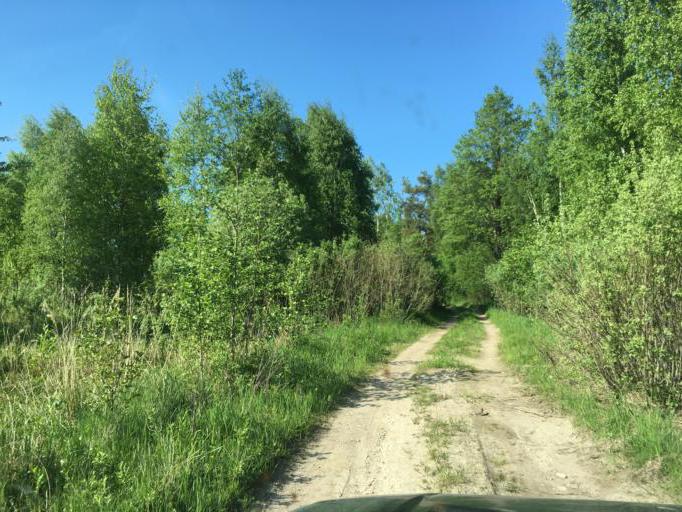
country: LV
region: Dundaga
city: Dundaga
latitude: 57.6010
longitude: 22.5073
